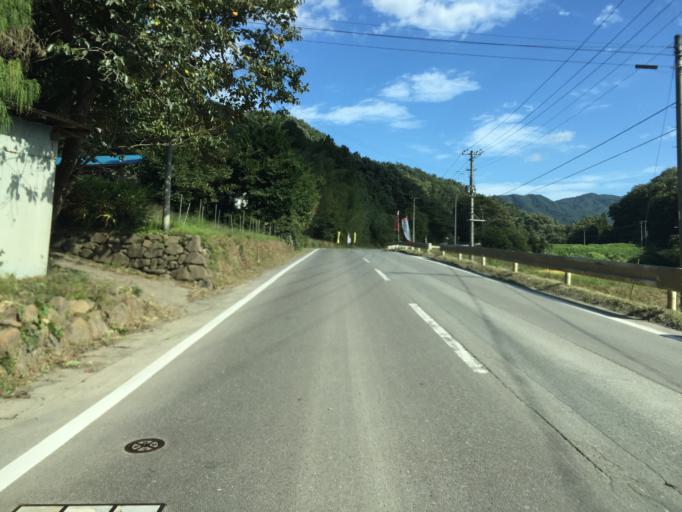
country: JP
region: Fukushima
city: Yanagawamachi-saiwaicho
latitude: 37.8564
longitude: 140.6406
